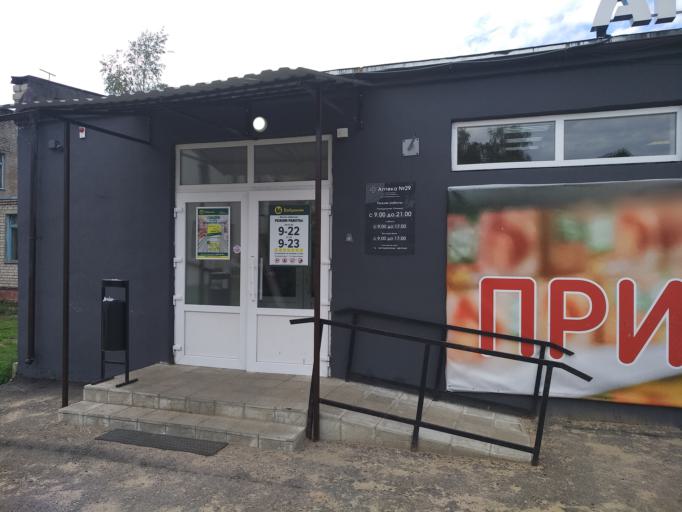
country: BY
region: Vitebsk
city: Mosar
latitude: 55.1473
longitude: 27.2067
